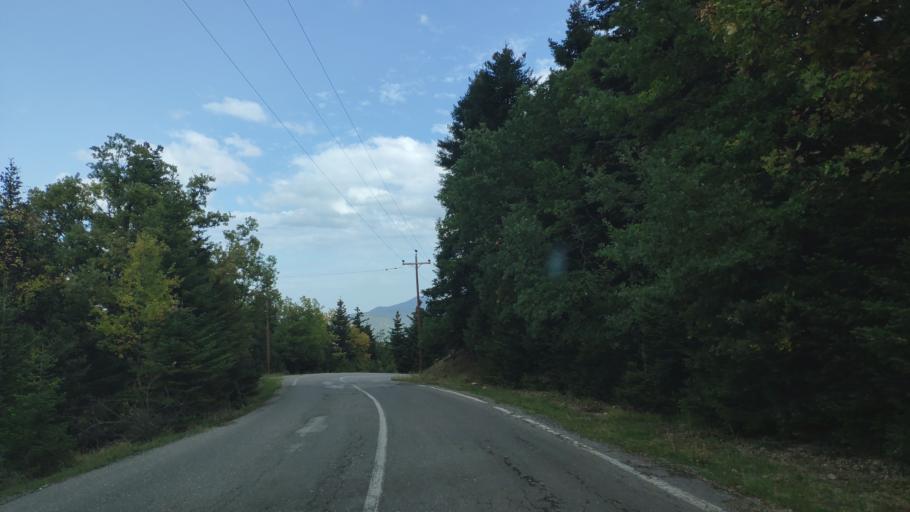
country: GR
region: Central Greece
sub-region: Nomos Fthiotidos
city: Anthili
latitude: 38.7368
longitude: 22.3771
